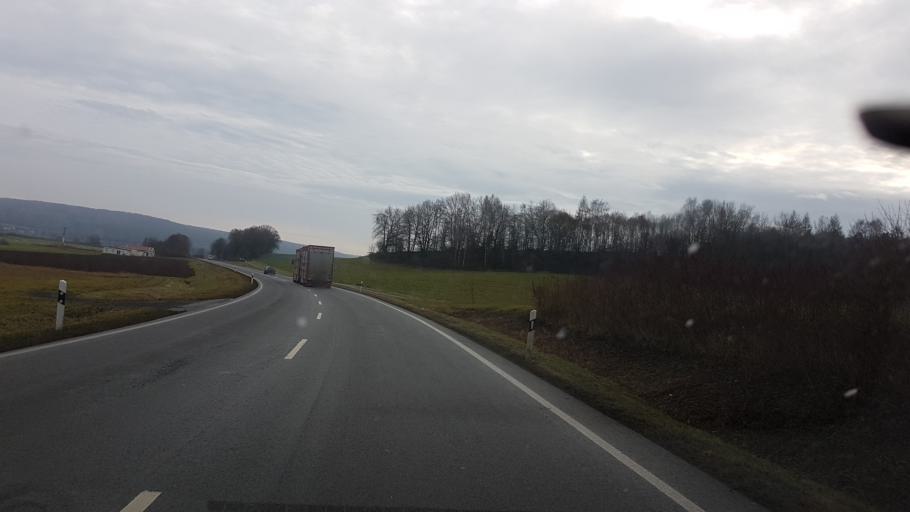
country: DE
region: Bavaria
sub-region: Upper Franconia
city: Gerach
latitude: 50.0431
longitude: 10.8142
